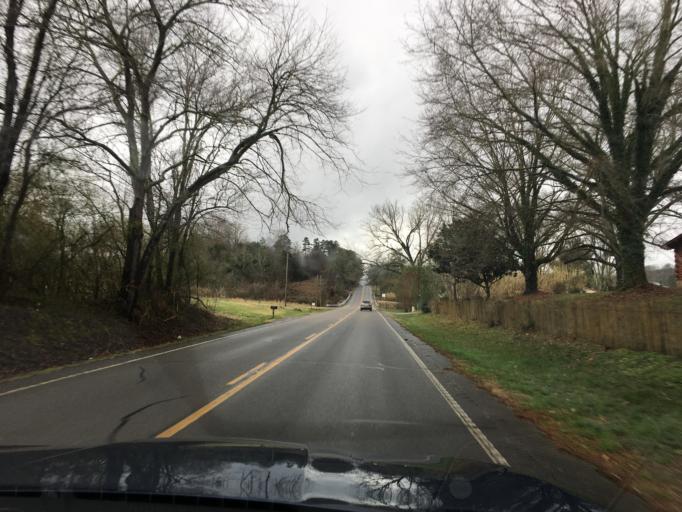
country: US
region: Tennessee
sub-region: Polk County
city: Benton
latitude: 35.1248
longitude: -84.6481
